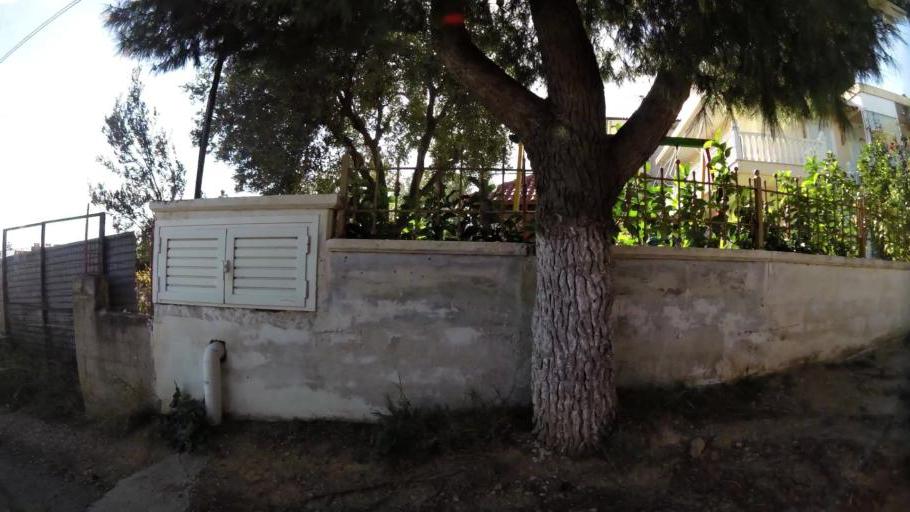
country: GR
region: Attica
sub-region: Nomarchia Anatolikis Attikis
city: Acharnes
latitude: 38.1078
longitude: 23.7186
